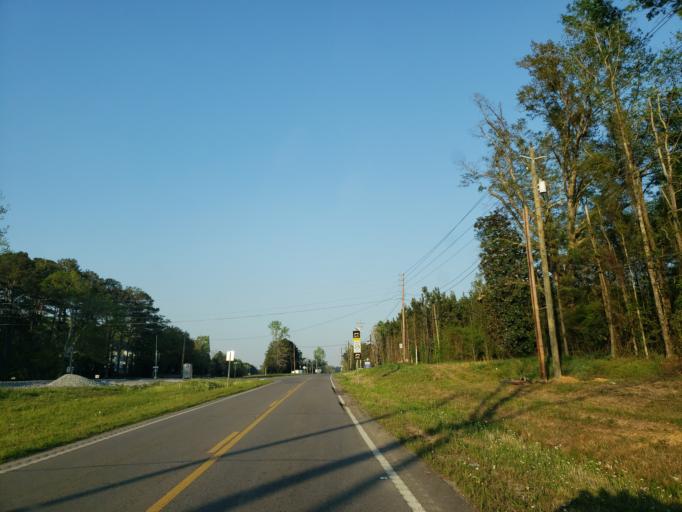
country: US
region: Mississippi
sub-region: Lauderdale County
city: Marion
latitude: 32.4026
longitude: -88.5969
